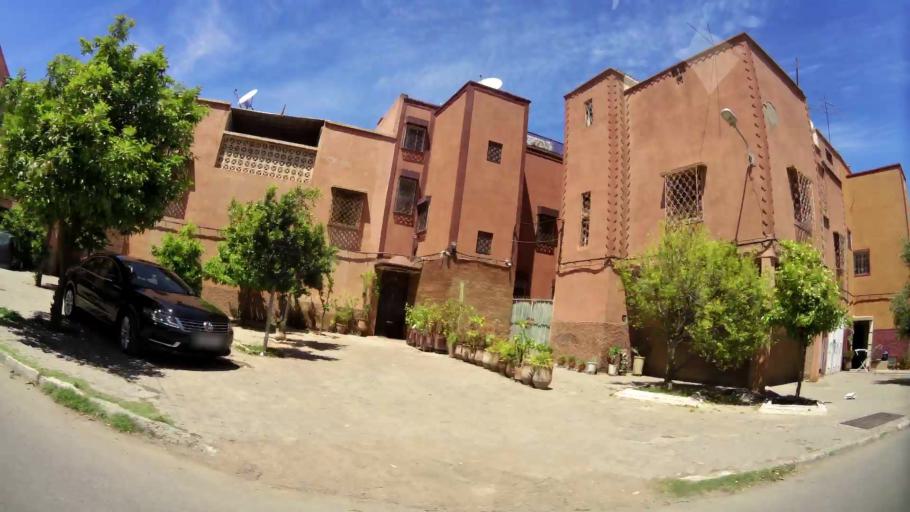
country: MA
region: Marrakech-Tensift-Al Haouz
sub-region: Marrakech
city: Marrakesh
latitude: 31.6347
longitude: -8.0466
